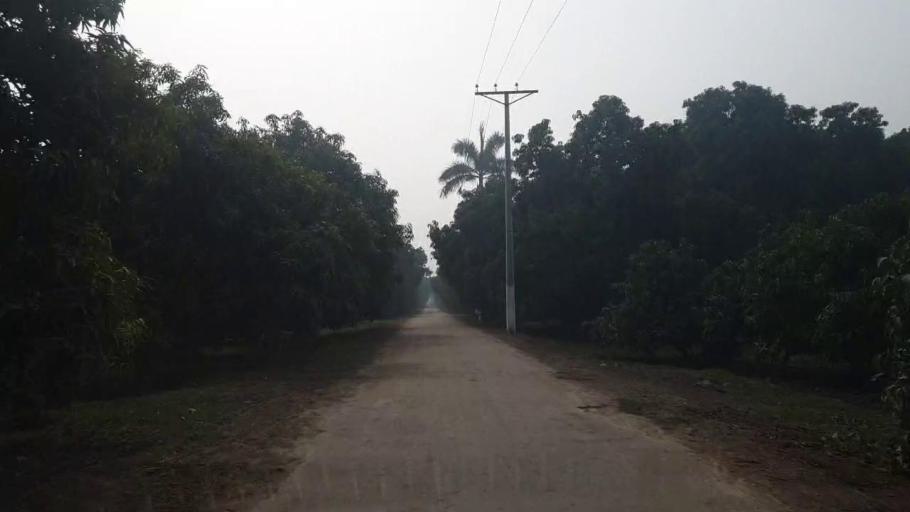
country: PK
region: Sindh
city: Tando Adam
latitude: 25.7888
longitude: 68.5962
